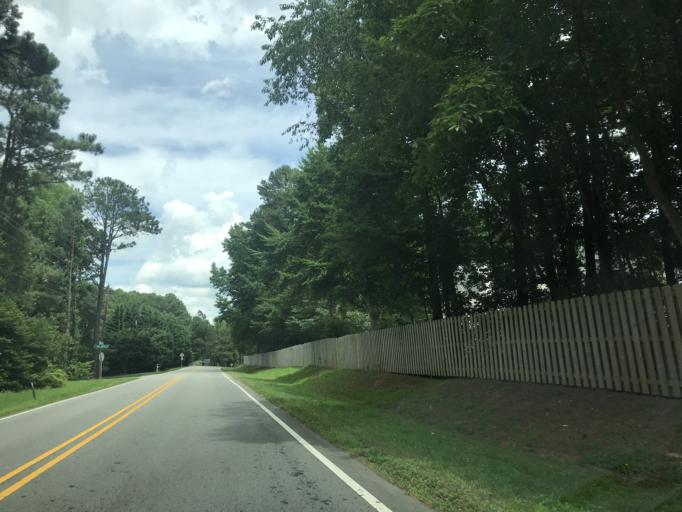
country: US
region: North Carolina
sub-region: Wake County
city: West Raleigh
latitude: 35.9131
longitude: -78.6930
